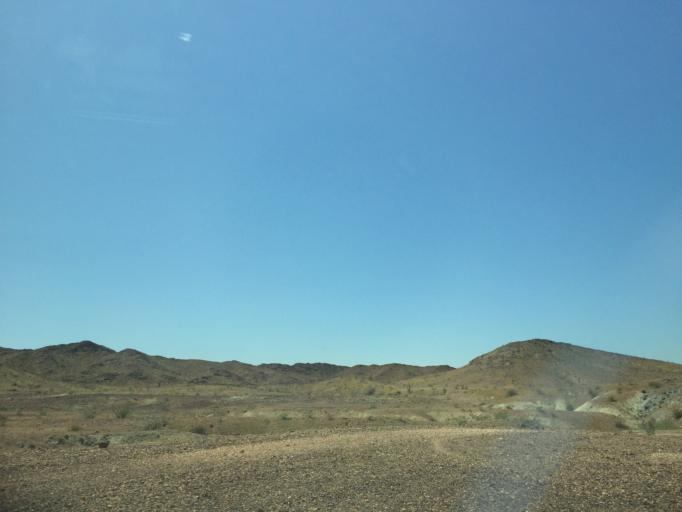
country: US
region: California
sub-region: Riverside County
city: Mesa Verde
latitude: 33.4071
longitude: -115.0593
